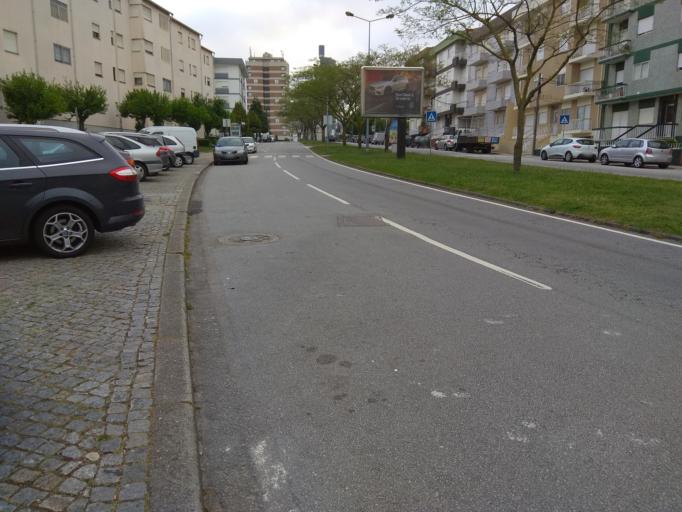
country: PT
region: Porto
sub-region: Maia
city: Maia
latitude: 41.2290
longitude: -8.6205
